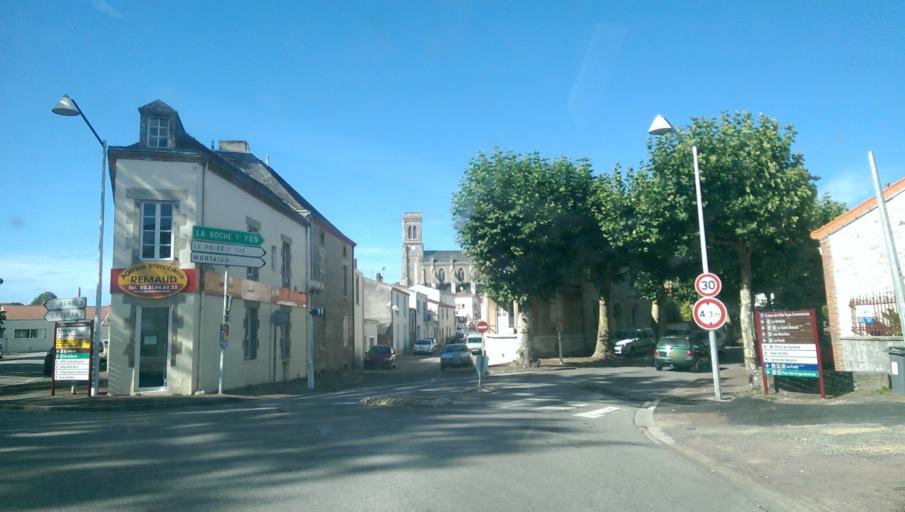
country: FR
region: Pays de la Loire
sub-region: Departement de la Vendee
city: Aizenay
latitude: 46.7379
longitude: -1.6099
